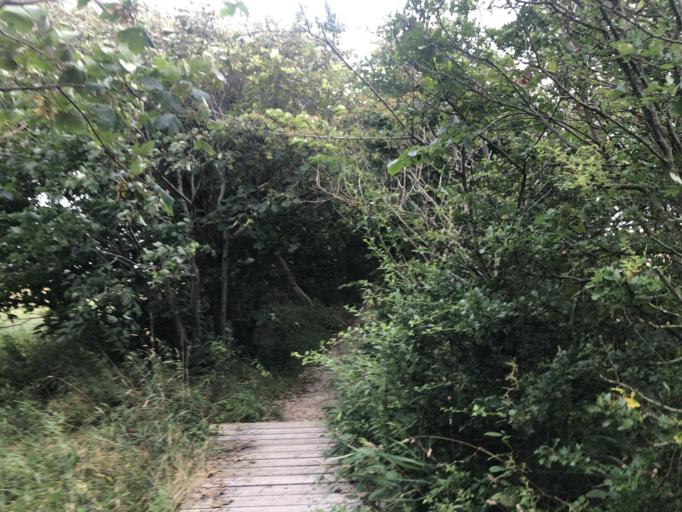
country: DK
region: Central Jutland
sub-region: Ringkobing-Skjern Kommune
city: Skjern
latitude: 55.9037
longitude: 8.4229
